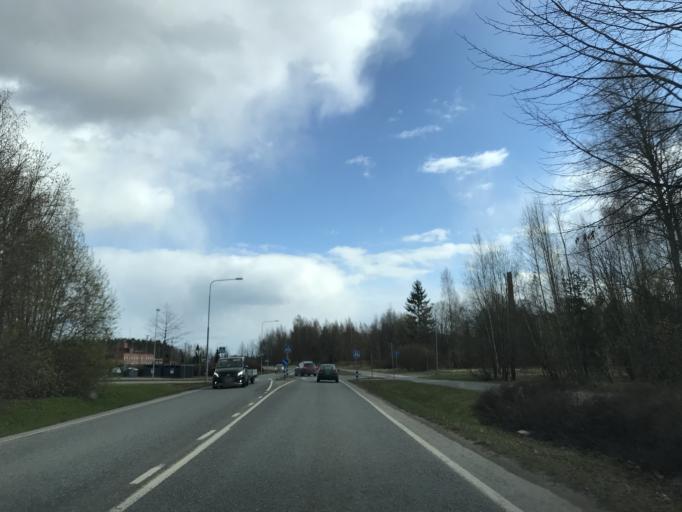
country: FI
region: Uusimaa
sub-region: Helsinki
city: Hyvinge
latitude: 60.5520
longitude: 24.9706
